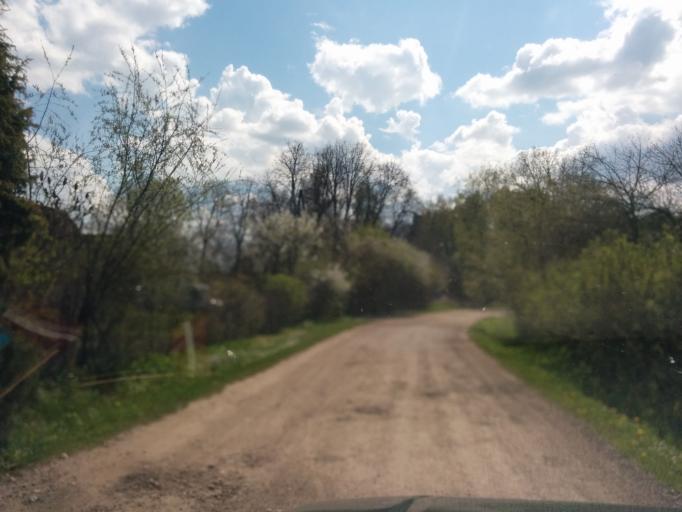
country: LV
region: Ozolnieku
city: Ozolnieki
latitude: 56.6296
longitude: 23.7762
